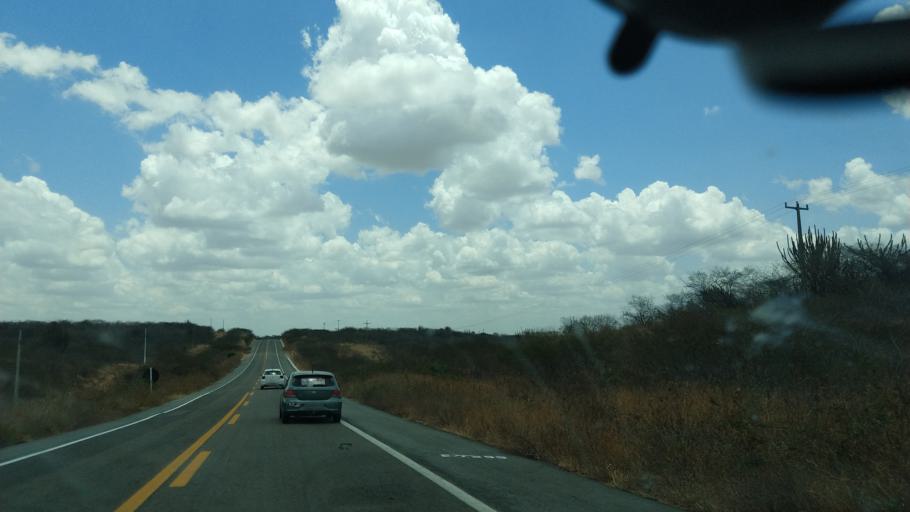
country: BR
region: Rio Grande do Norte
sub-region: Cerro Cora
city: Cerro Cora
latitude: -6.2018
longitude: -36.2743
